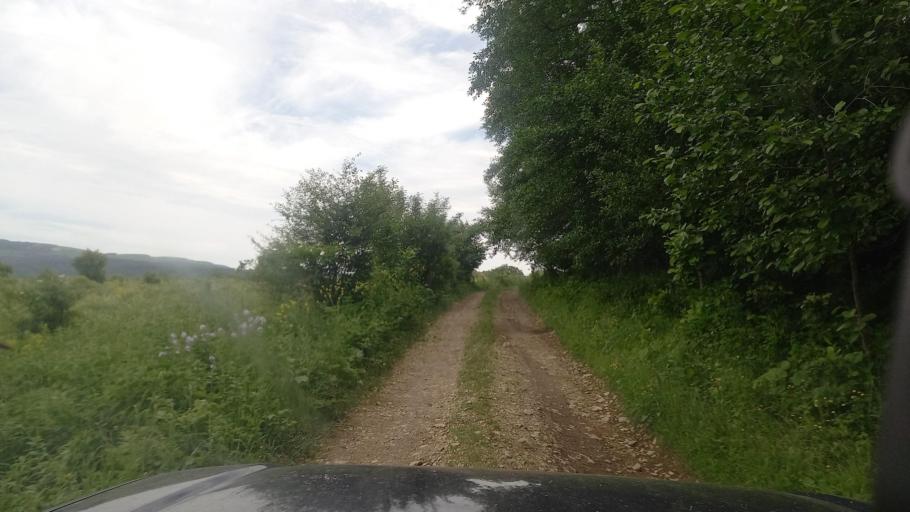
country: RU
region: Karachayevo-Cherkesiya
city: Pregradnaya
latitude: 44.0900
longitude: 41.1825
